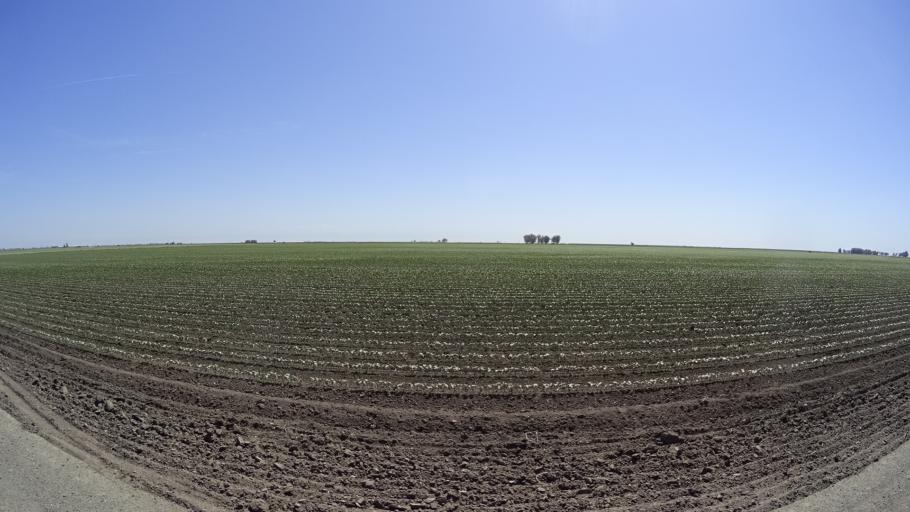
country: US
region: California
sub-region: Kings County
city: Stratford
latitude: 36.1873
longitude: -119.7803
